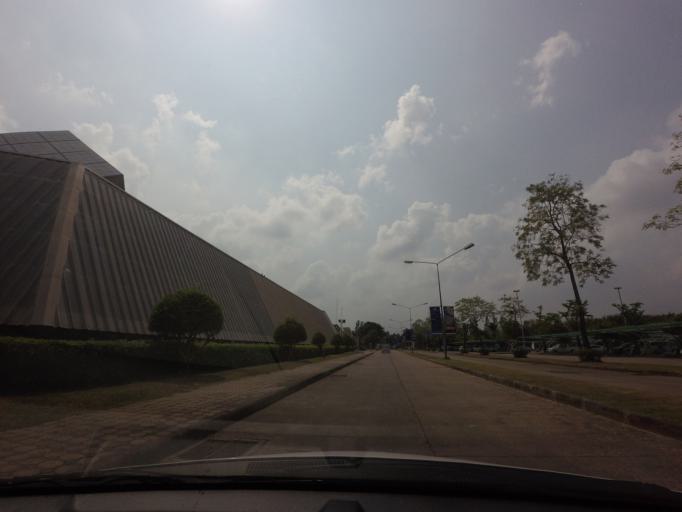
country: TH
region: Pathum Thani
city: Thanyaburi
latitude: 14.0493
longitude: 100.7167
